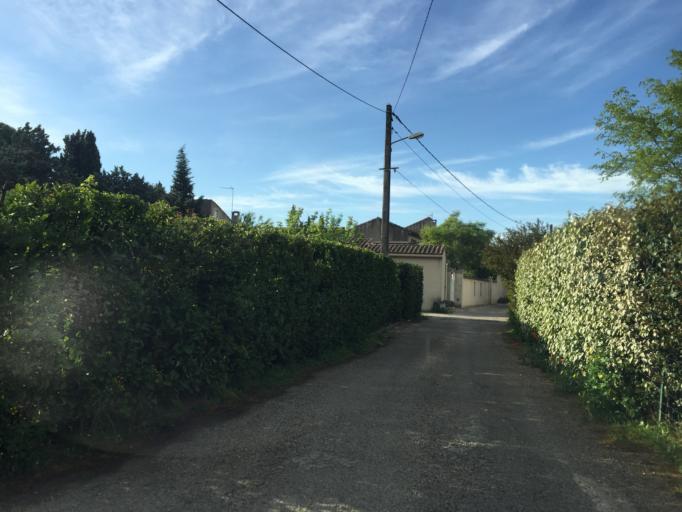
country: FR
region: Provence-Alpes-Cote d'Azur
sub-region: Departement du Vaucluse
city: Sorgues
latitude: 44.0126
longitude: 4.8838
